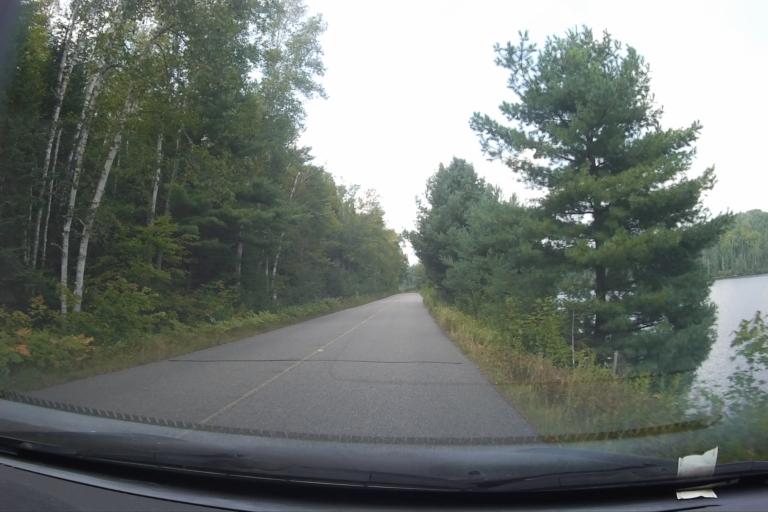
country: CA
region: Ontario
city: Bancroft
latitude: 45.5955
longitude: -78.3268
